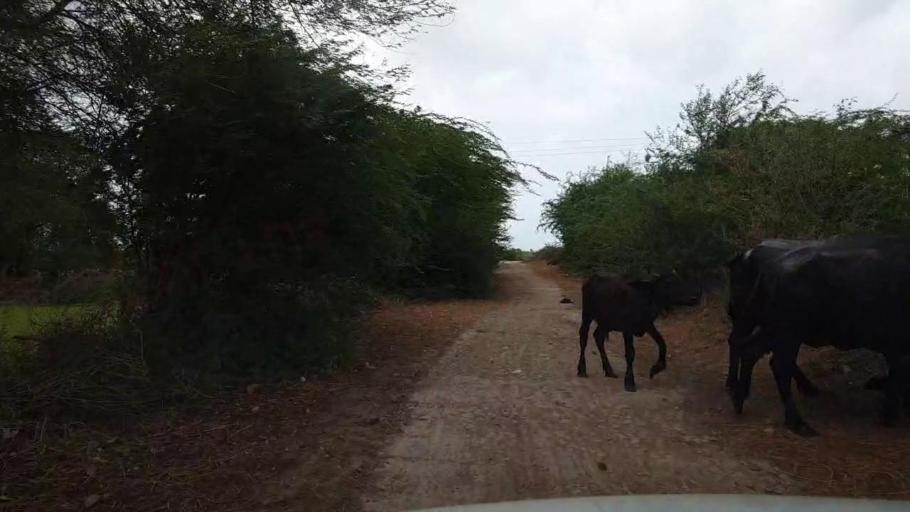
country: PK
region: Sindh
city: Kario
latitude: 24.6894
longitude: 68.6664
